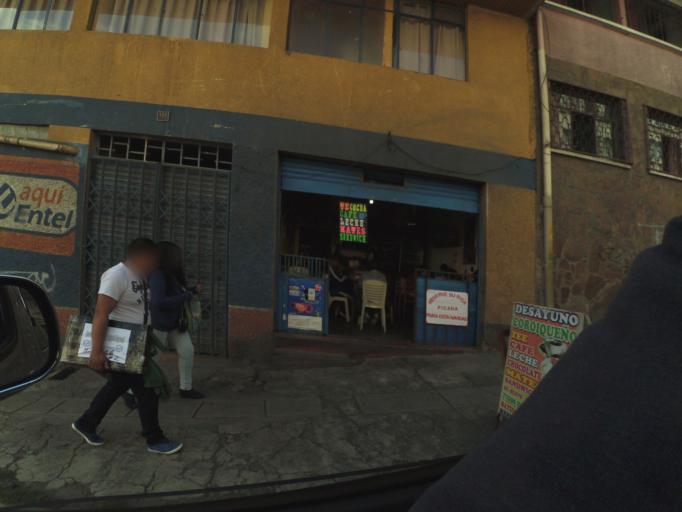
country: BO
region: La Paz
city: La Paz
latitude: -16.4923
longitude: -68.1422
